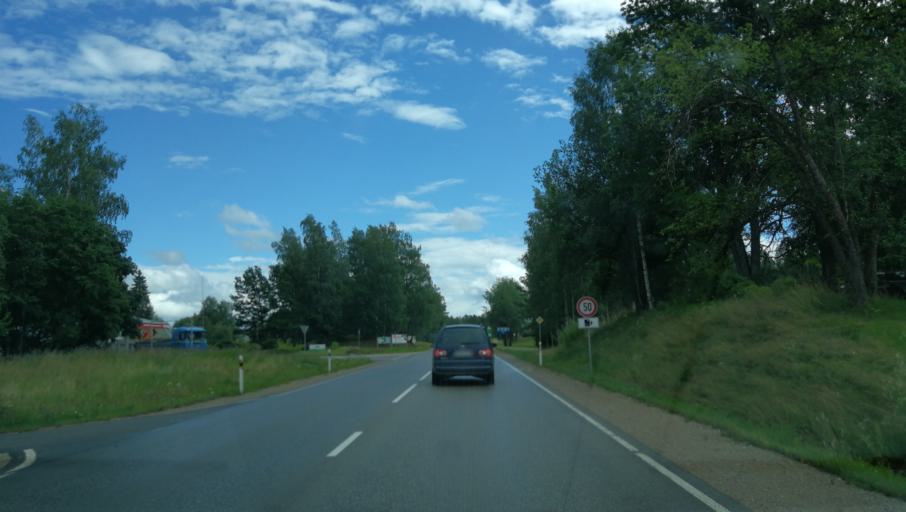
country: LV
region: Vecpiebalga
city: Vecpiebalga
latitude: 57.0645
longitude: 25.8056
